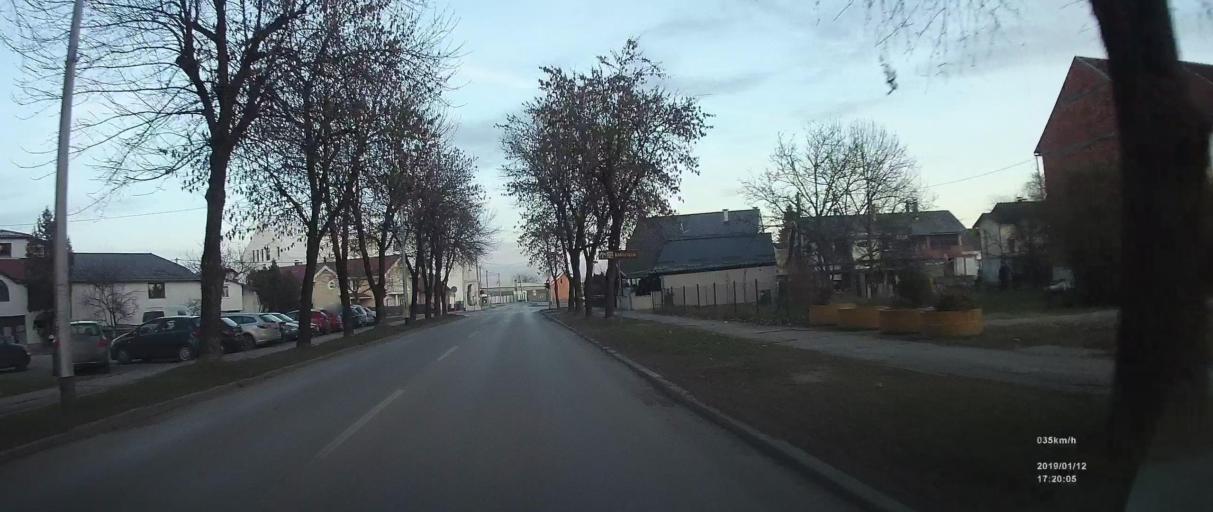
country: HR
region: Zagrebacka
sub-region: Grad Velika Gorica
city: Velika Gorica
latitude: 45.7177
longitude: 16.0751
